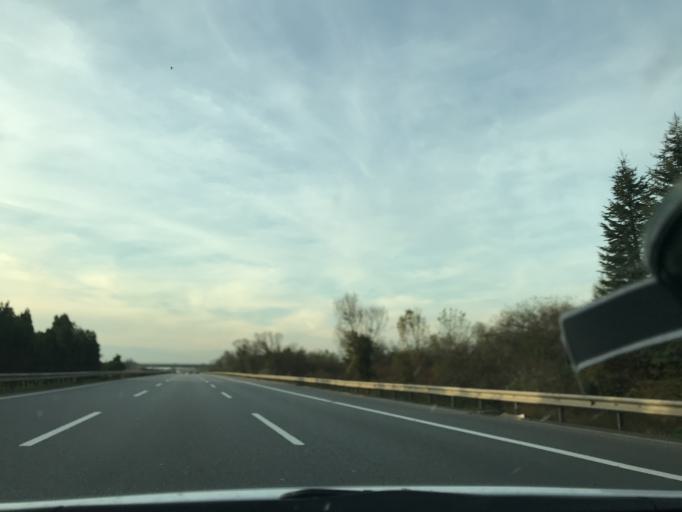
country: TR
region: Duzce
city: Cilimli
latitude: 40.8394
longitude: 31.0277
